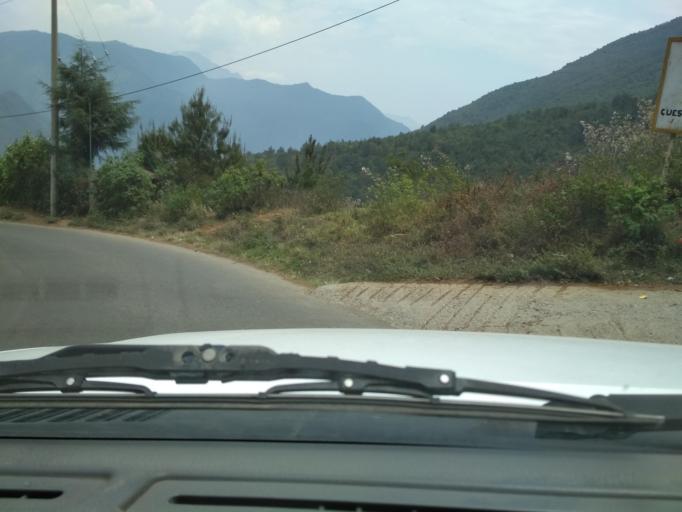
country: MX
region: Veracruz
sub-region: Camerino Z. Mendoza
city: La Cuesta
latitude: 18.7885
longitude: -97.1643
